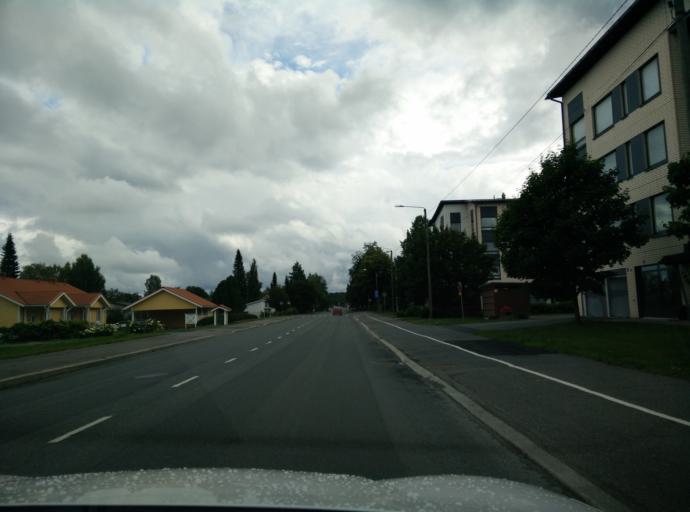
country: FI
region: Haeme
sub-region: Haemeenlinna
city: Haemeenlinna
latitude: 60.9993
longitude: 24.4268
